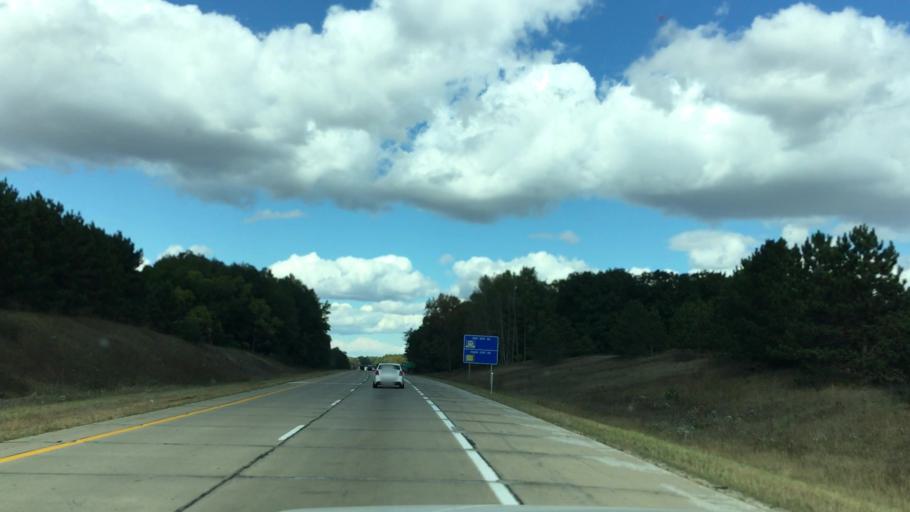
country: US
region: Michigan
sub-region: Eaton County
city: Olivet
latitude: 42.4264
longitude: -84.9559
